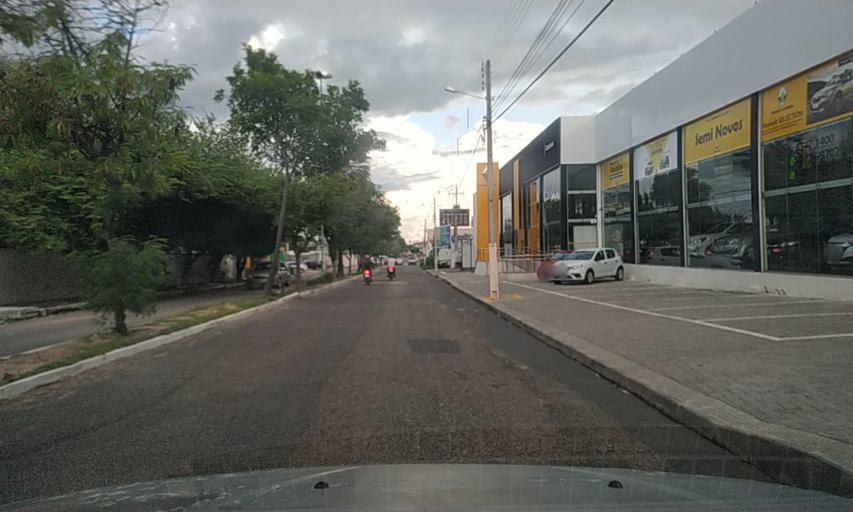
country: BR
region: Rio Grande do Norte
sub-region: Mossoro
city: Mossoro
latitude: -5.1859
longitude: -37.3542
